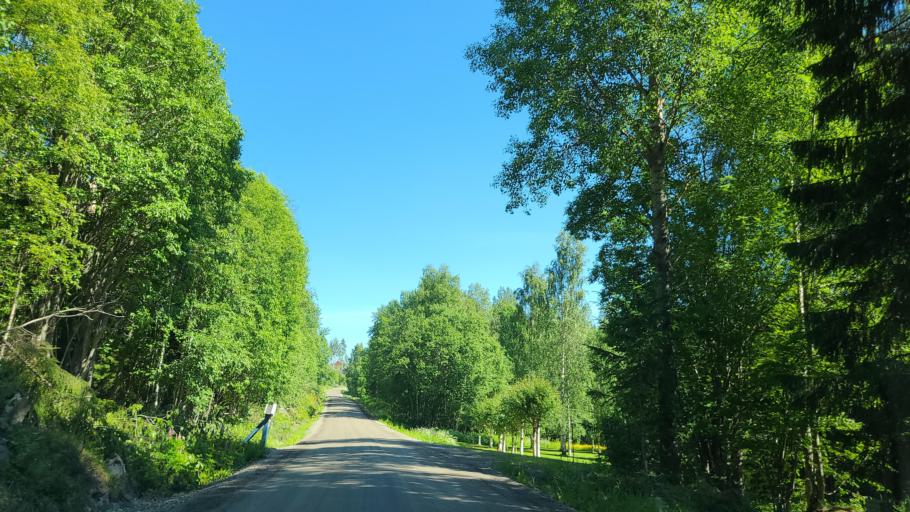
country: SE
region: Vaesterbotten
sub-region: Bjurholms Kommun
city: Bjurholm
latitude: 63.6760
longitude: 19.0159
